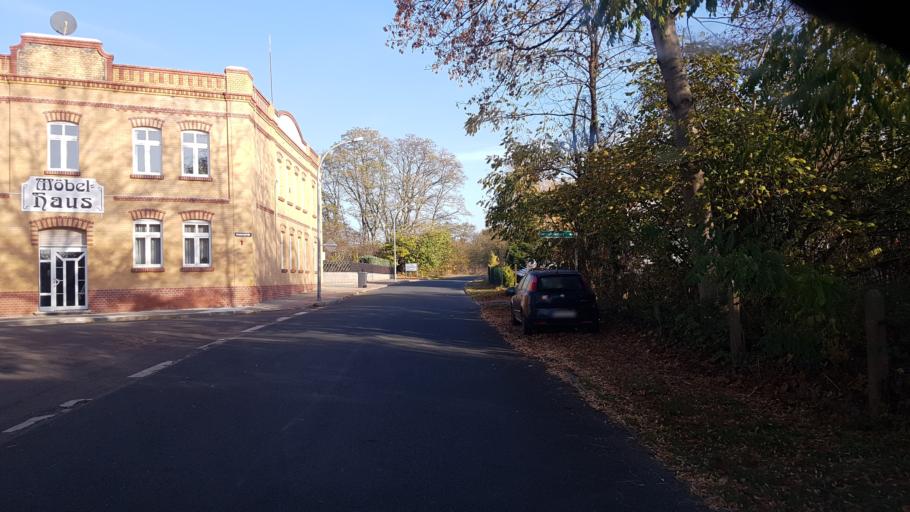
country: DE
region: Brandenburg
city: Schipkau
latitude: 51.5621
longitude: 13.8974
